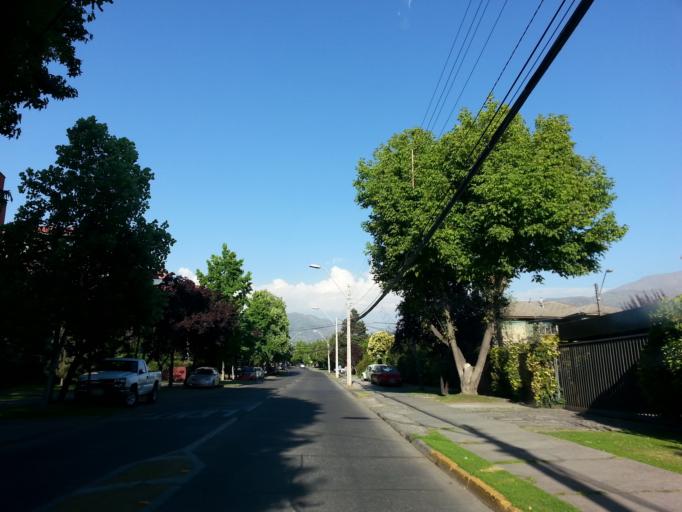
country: CL
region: Santiago Metropolitan
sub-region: Provincia de Santiago
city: Villa Presidente Frei, Nunoa, Santiago, Chile
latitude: -33.3852
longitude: -70.5451
